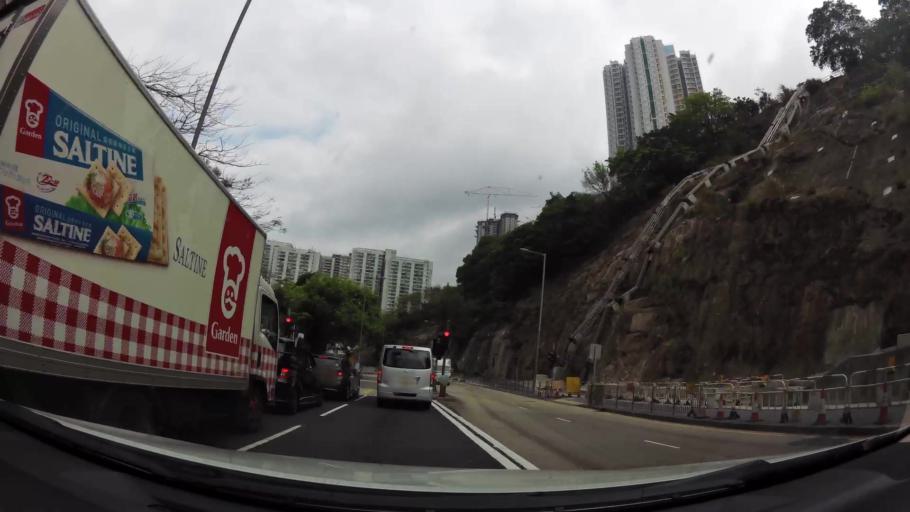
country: HK
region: Kowloon City
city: Kowloon
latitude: 22.3234
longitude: 114.2303
